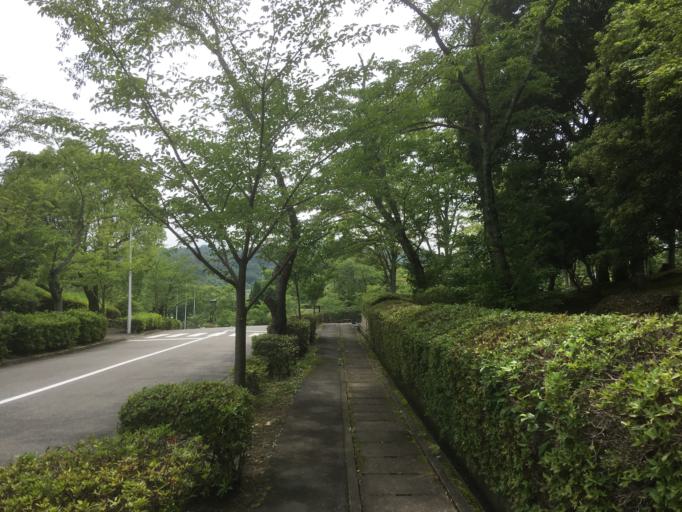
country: JP
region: Nara
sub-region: Ikoma-shi
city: Ikoma
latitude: 34.7375
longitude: 135.6930
